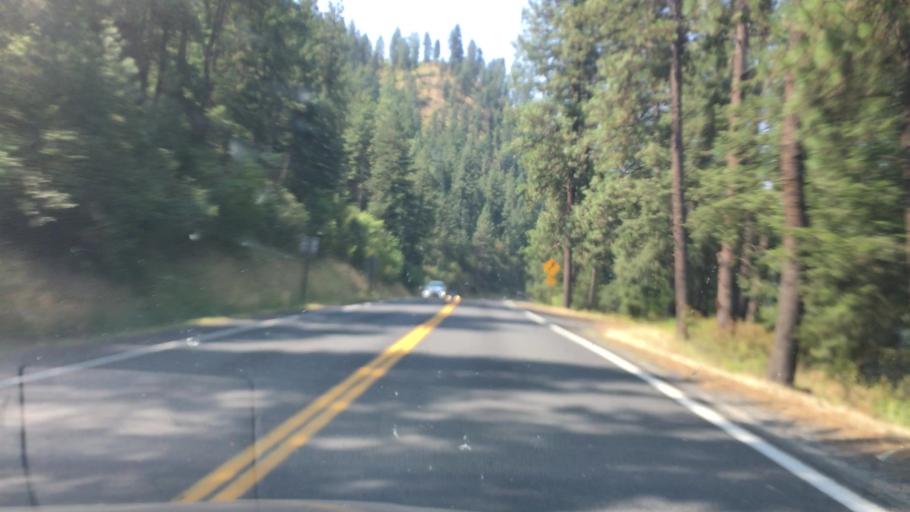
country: US
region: Idaho
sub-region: Clearwater County
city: Orofino
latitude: 46.4998
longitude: -116.3936
